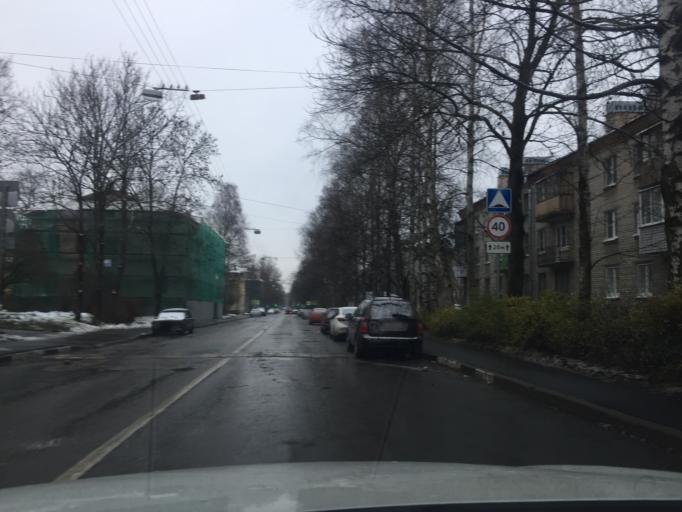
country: RU
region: St.-Petersburg
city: Pushkin
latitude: 59.7231
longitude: 30.4025
